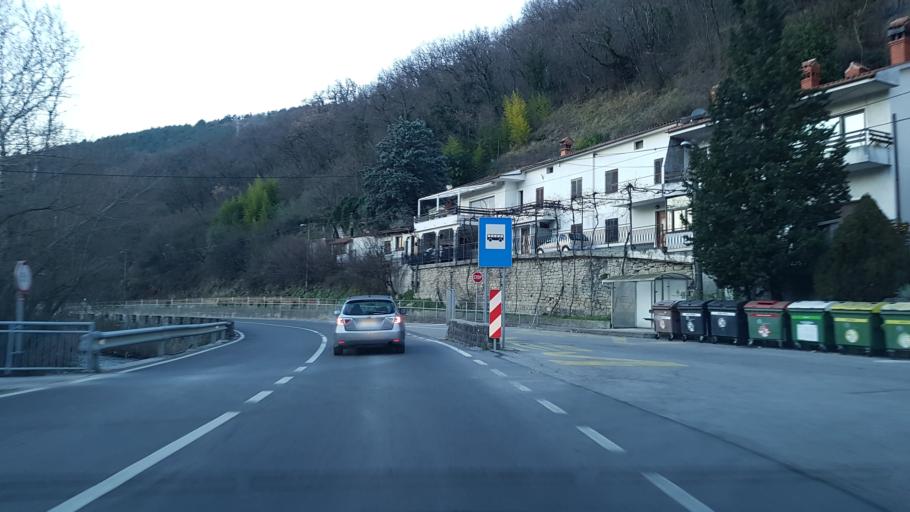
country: SI
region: Koper-Capodistria
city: Sv. Anton
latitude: 45.5438
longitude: 13.8477
